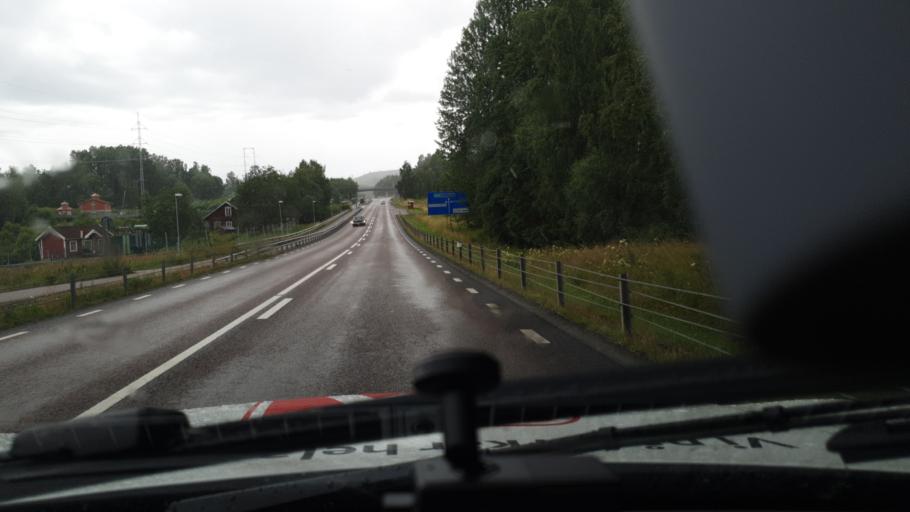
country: SE
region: Vaermland
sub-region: Sunne Kommun
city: Sunne
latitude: 59.7949
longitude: 13.1049
